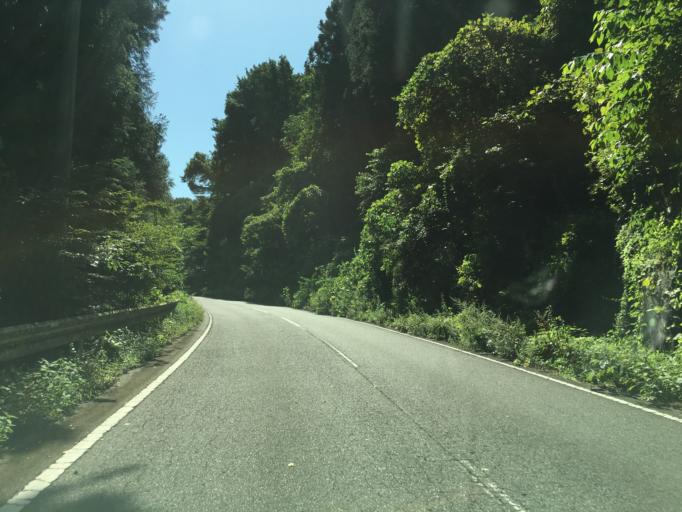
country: JP
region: Fukushima
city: Sukagawa
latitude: 37.2920
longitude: 140.4877
